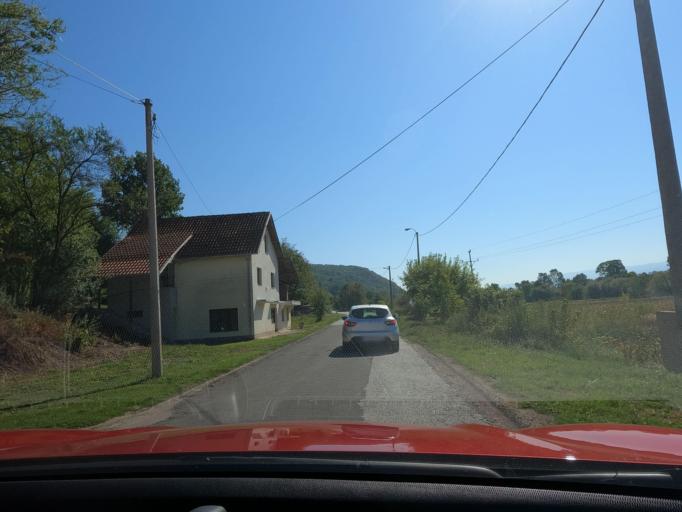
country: RS
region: Central Serbia
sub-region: Raski Okrug
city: Kraljevo
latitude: 43.7413
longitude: 20.7313
